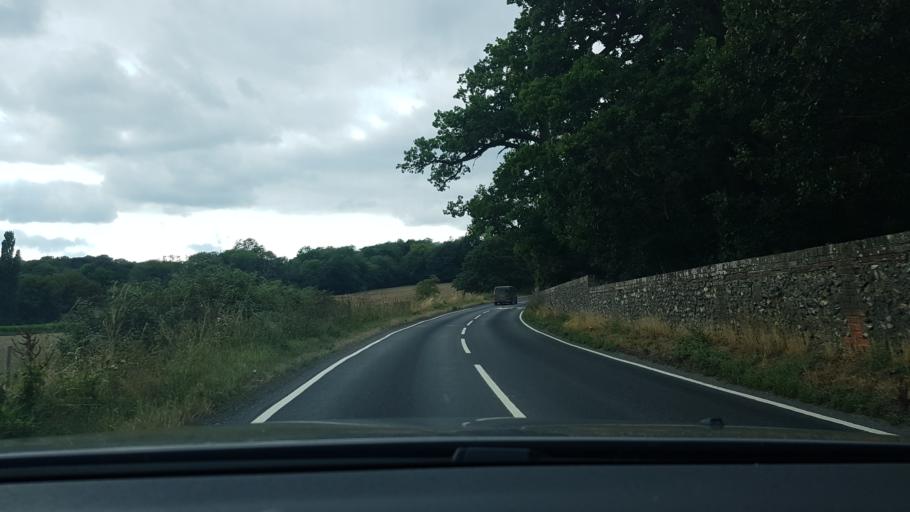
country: GB
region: England
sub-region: West Berkshire
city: Theale
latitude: 51.4373
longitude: -1.1081
